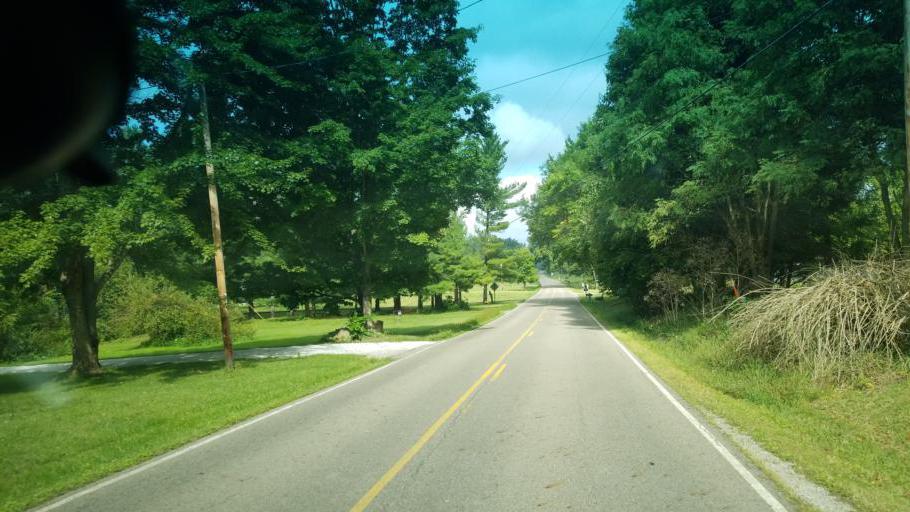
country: US
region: Ohio
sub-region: Licking County
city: Johnstown
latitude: 40.1979
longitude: -82.6036
